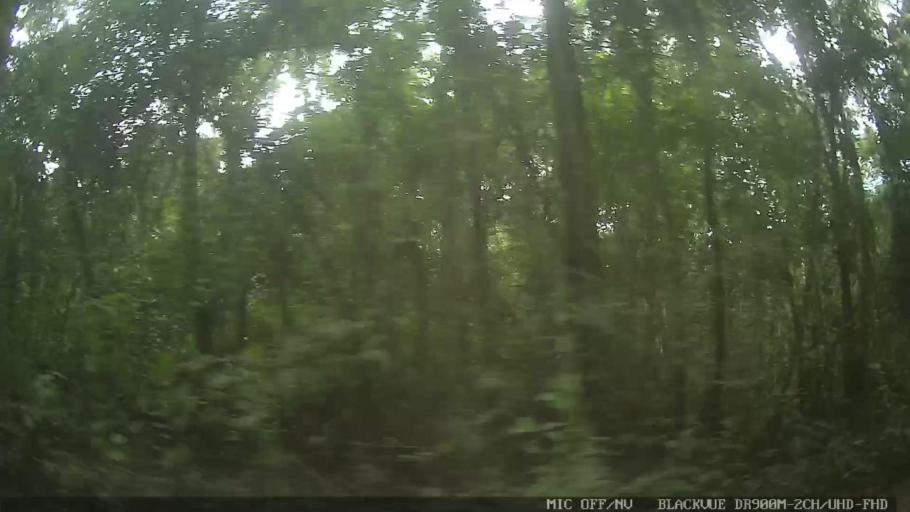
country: BR
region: Sao Paulo
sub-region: Bom Jesus Dos Perdoes
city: Bom Jesus dos Perdoes
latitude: -23.1428
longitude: -46.5112
